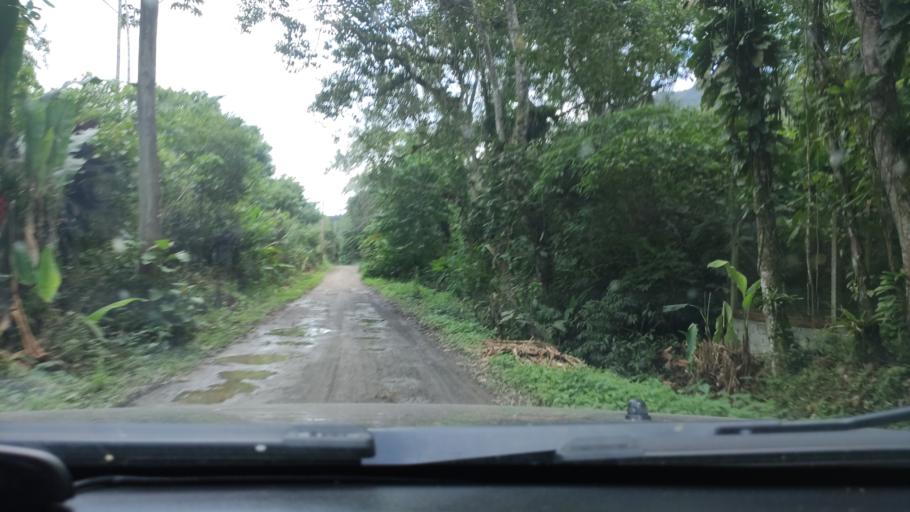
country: BR
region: Sao Paulo
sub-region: Sao Sebastiao
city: Sao Sebastiao
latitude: -23.7272
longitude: -45.4927
